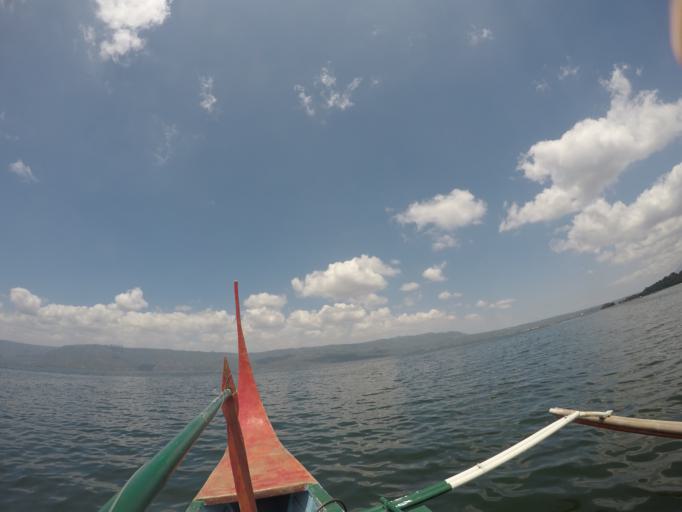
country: PH
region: Calabarzon
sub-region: Province of Batangas
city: Talisay
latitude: 14.0361
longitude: 121.0032
